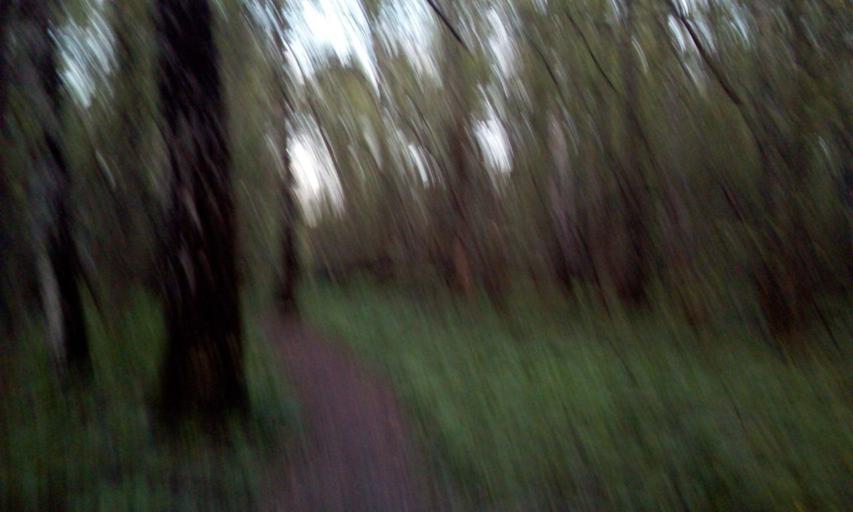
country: RU
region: Moscow
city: Tyoply Stan
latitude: 55.6381
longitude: 37.4886
